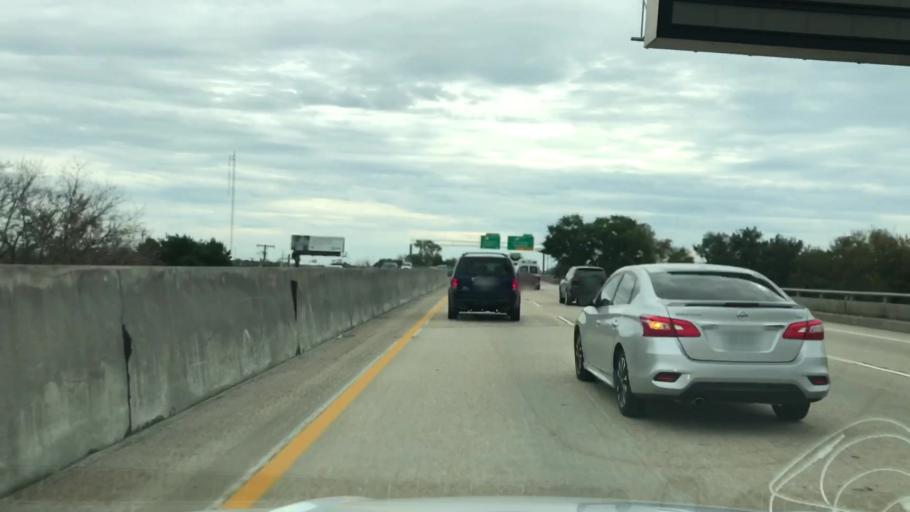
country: US
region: South Carolina
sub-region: Charleston County
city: Charleston
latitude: 32.8121
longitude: -79.9525
